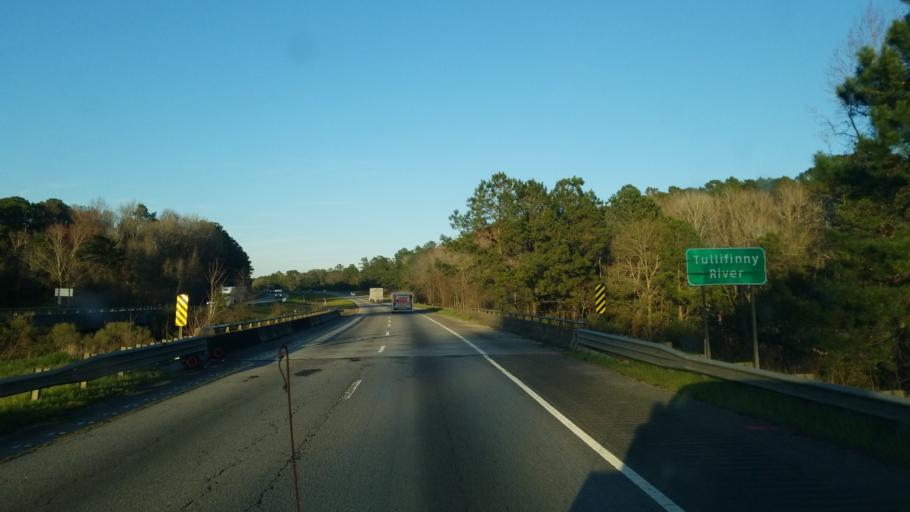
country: US
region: South Carolina
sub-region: Hampton County
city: Yemassee
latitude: 32.5997
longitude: -80.9029
